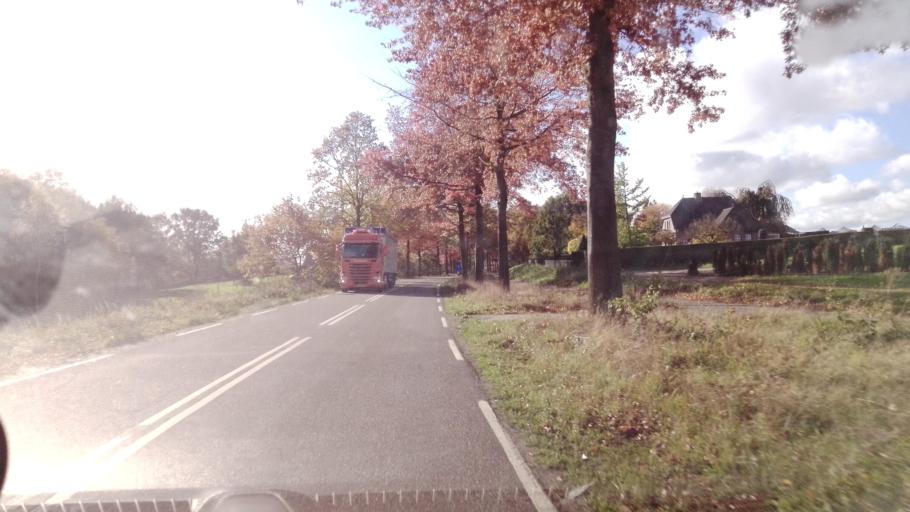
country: NL
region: Limburg
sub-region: Gemeente Venlo
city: Arcen
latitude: 51.4498
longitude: 6.1529
